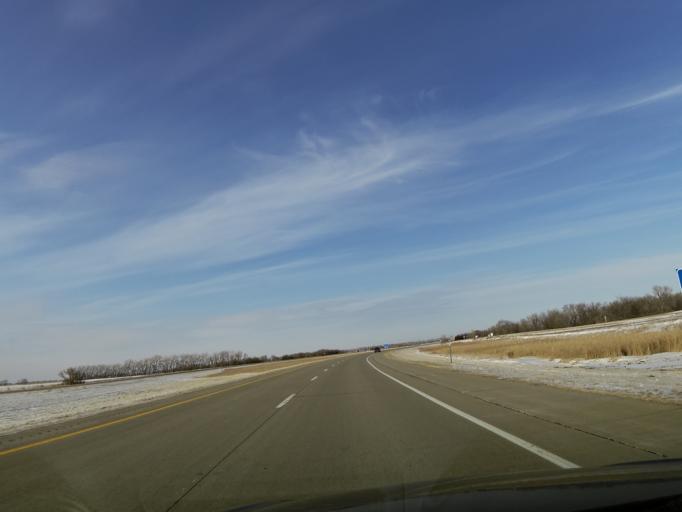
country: US
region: North Dakota
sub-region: Walsh County
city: Grafton
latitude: 48.4504
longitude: -97.1939
